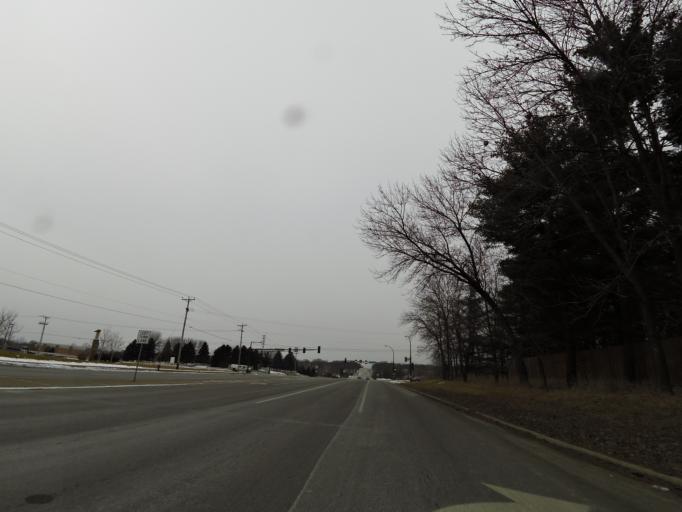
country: US
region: Minnesota
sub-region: Washington County
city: Woodbury
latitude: 44.9199
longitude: -92.9019
